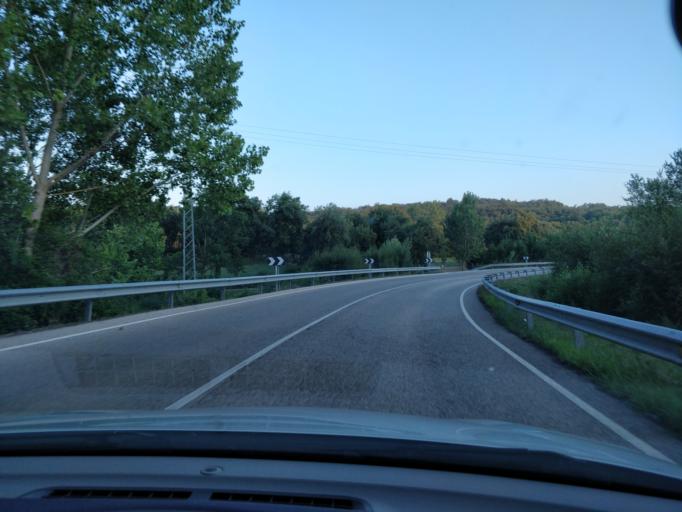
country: ES
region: Castille and Leon
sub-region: Provincia de Burgos
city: Medina de Pomar
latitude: 42.9639
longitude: -3.5476
